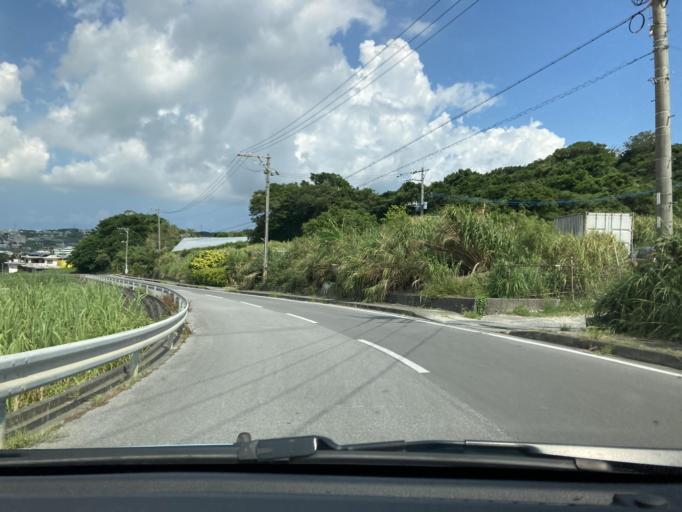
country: JP
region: Okinawa
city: Tomigusuku
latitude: 26.1487
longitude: 127.7589
